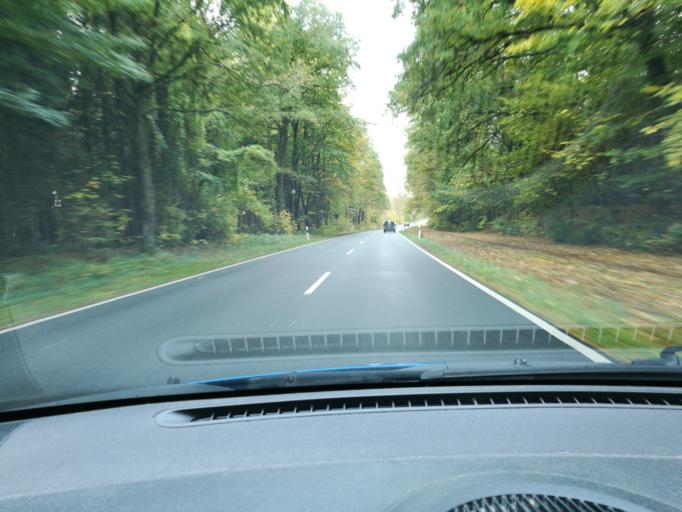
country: DE
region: Schleswig-Holstein
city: Gross Sarau
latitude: 53.7793
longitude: 10.7490
